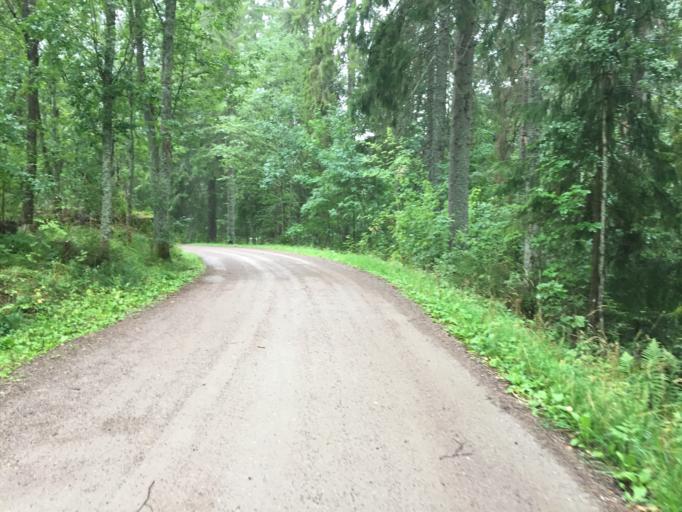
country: NO
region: Akershus
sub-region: Baerum
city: Lysaker
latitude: 59.9755
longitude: 10.6333
